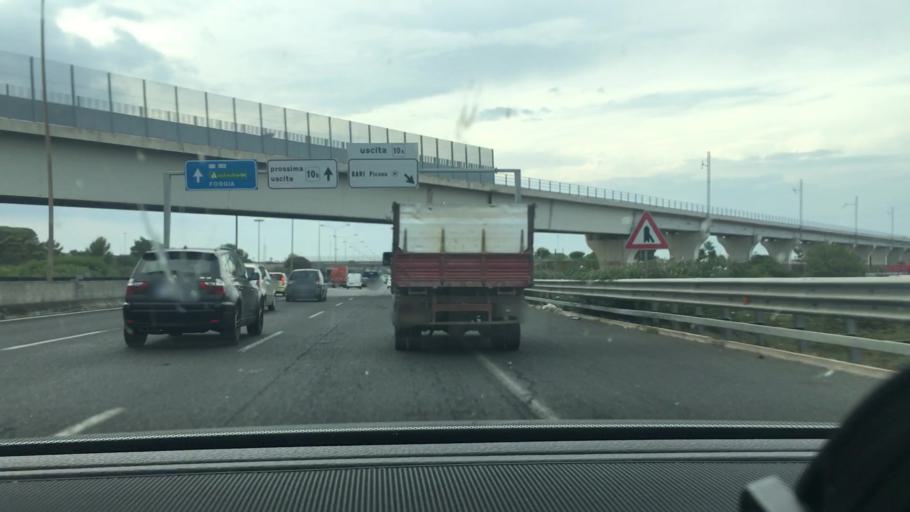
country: IT
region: Apulia
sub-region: Provincia di Bari
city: Bari
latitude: 41.0926
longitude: 16.8443
